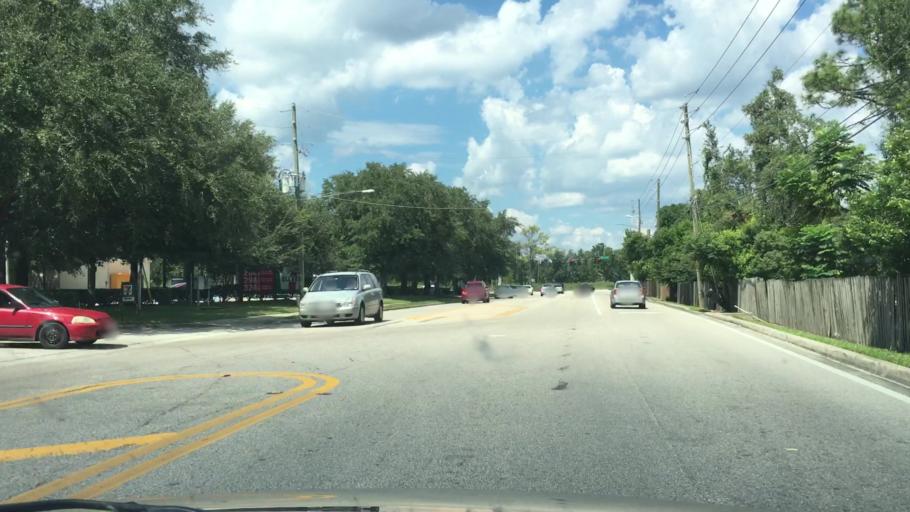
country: US
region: Florida
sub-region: Orange County
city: Lockhart
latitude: 28.6383
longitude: -81.4436
